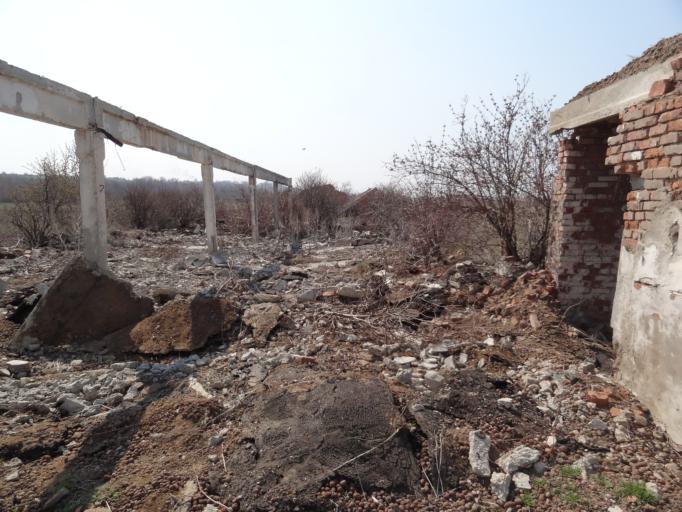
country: RU
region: Saratov
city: Privolzhskiy
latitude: 51.2446
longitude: 45.9284
